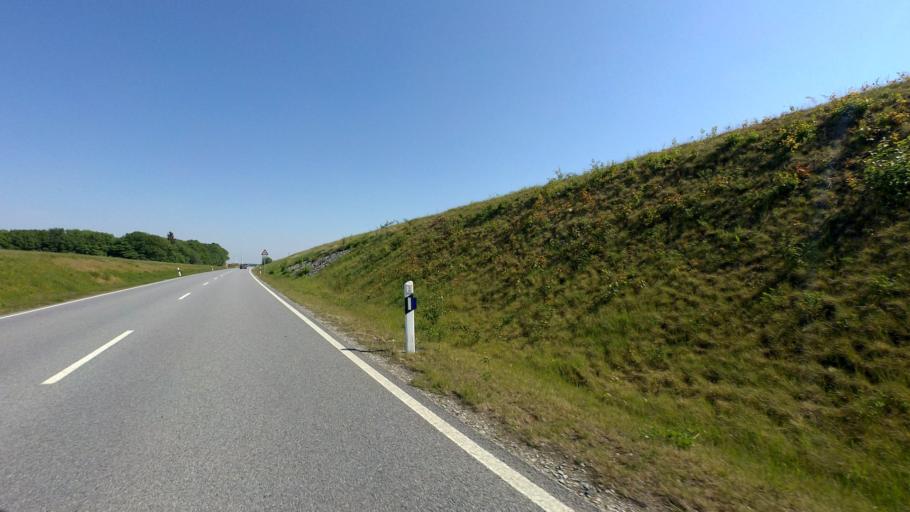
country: DE
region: Saxony
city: Elstra
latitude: 51.2046
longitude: 14.1506
